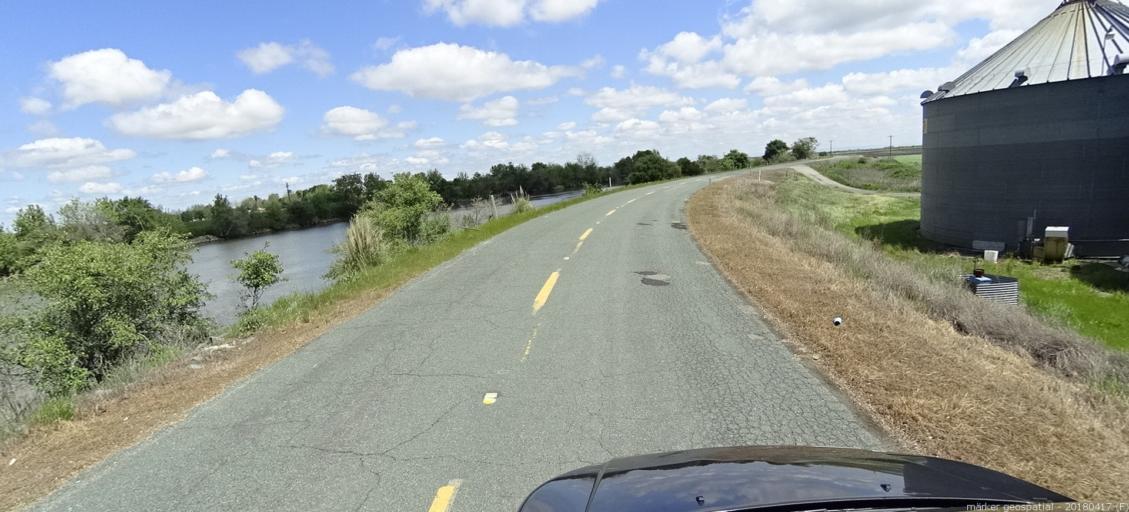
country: US
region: California
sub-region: Solano County
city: Rio Vista
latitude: 38.1569
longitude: -121.5907
